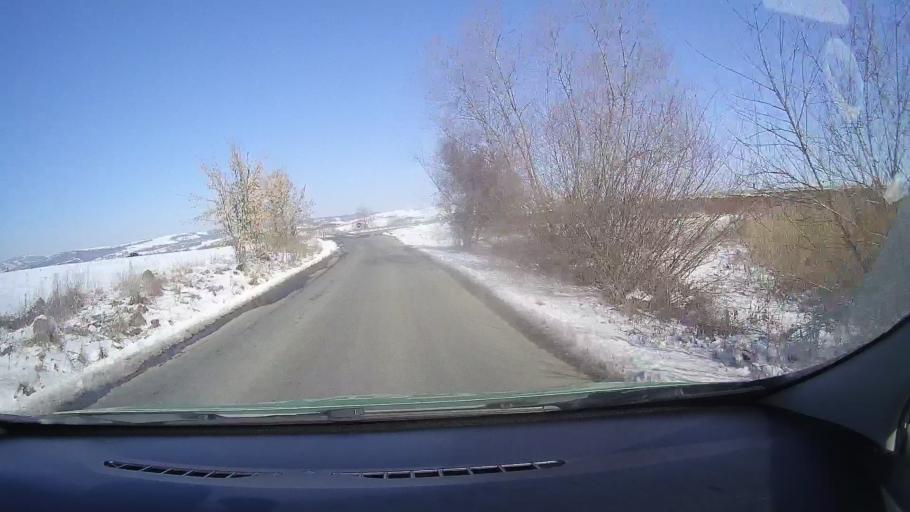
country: RO
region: Brasov
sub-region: Comuna Mandra
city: Mandra
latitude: 45.8315
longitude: 25.0139
